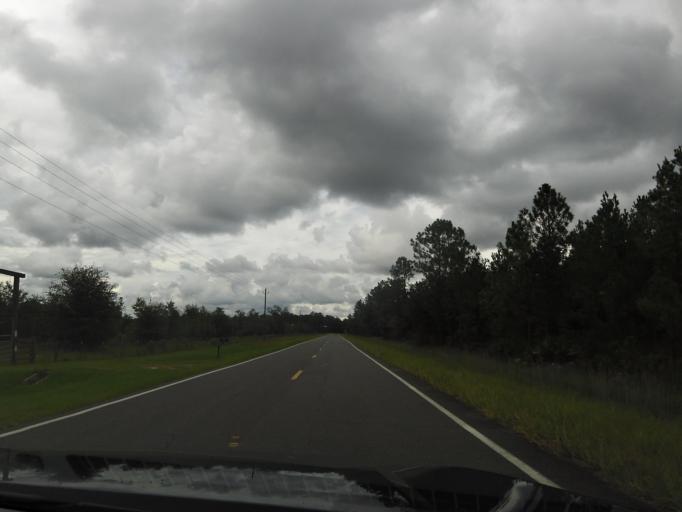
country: US
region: Florida
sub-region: Baker County
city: Macclenny
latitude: 30.4797
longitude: -82.1988
